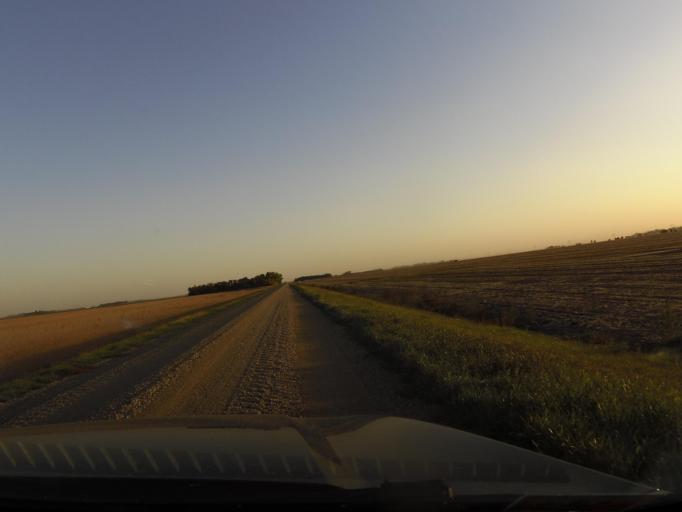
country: US
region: North Dakota
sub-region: Walsh County
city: Grafton
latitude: 48.3969
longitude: -97.2556
